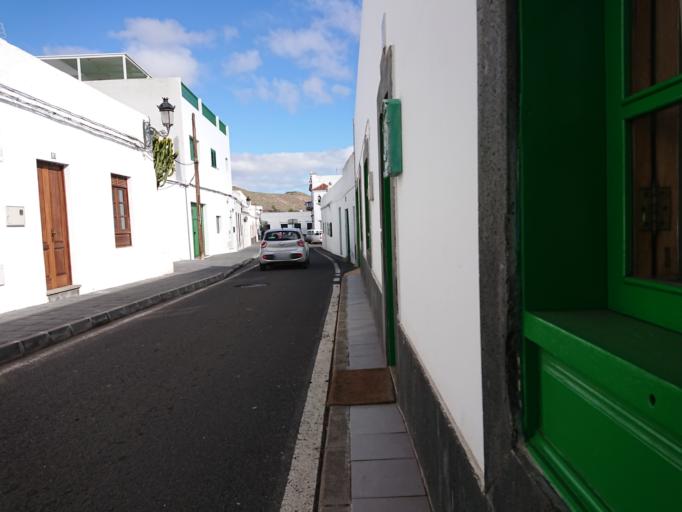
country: ES
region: Canary Islands
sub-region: Provincia de Las Palmas
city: Haria
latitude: 29.1458
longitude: -13.5010
